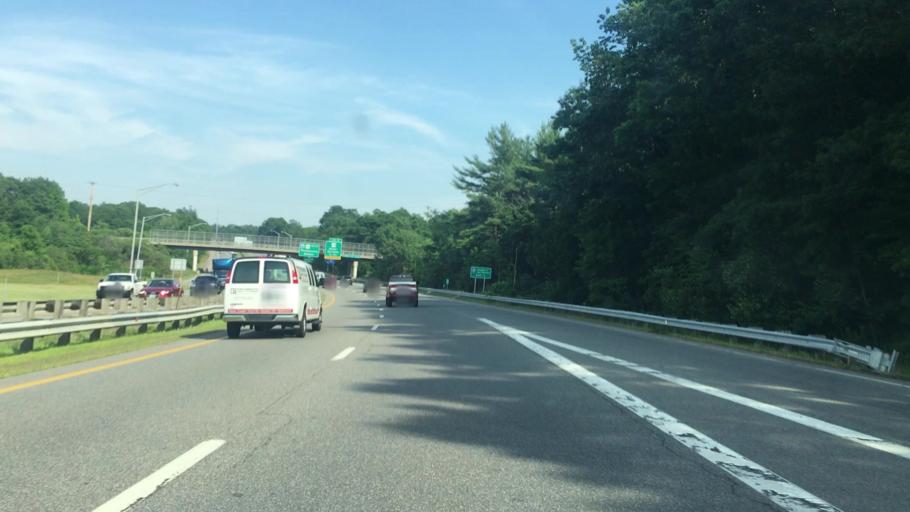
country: US
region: New Hampshire
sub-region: Strafford County
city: Dover
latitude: 43.1837
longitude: -70.8850
